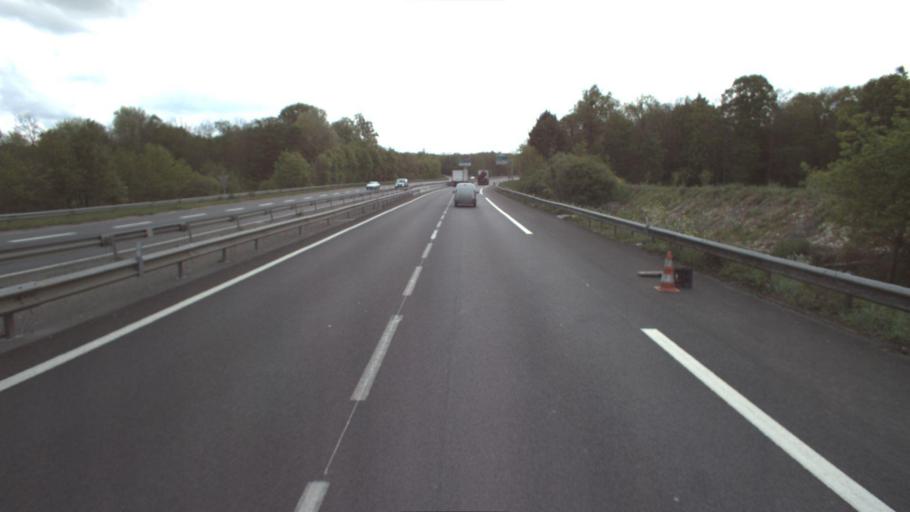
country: FR
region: Ile-de-France
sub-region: Departement de Seine-et-Marne
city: Fontenay-Tresigny
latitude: 48.7207
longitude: 2.8416
